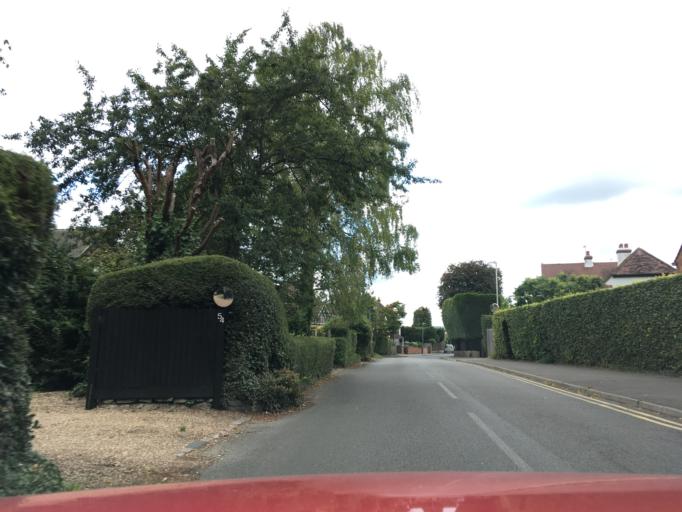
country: GB
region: England
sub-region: Kent
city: Maidstone
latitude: 51.2487
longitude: 0.5306
